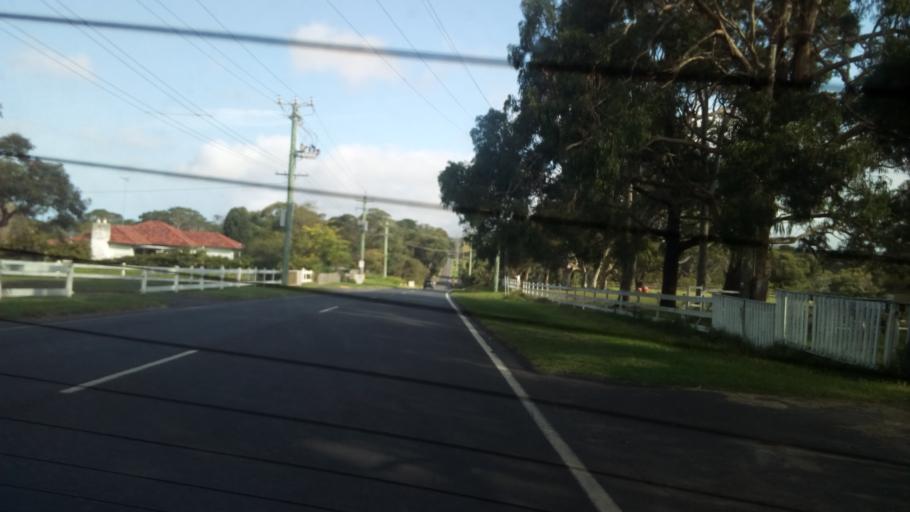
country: AU
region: New South Wales
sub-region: Wollongong
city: Helensburgh
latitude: -34.2051
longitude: 150.9791
